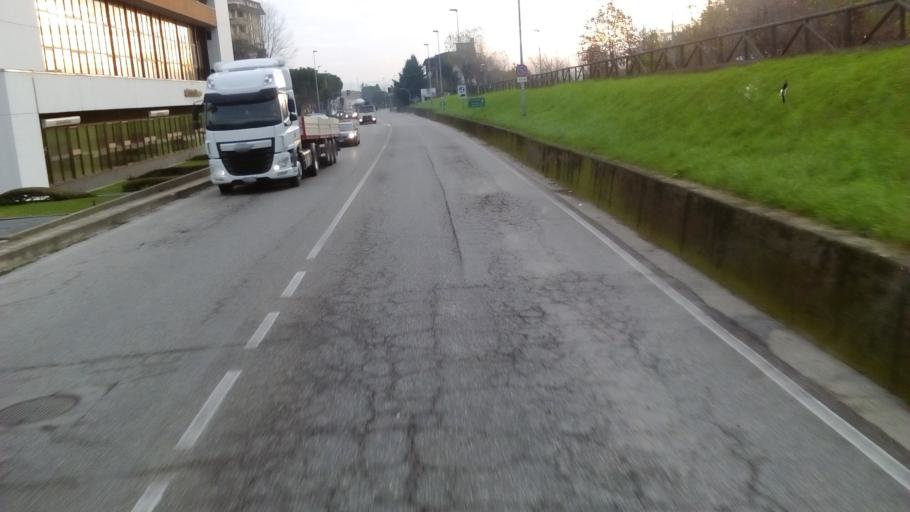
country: IT
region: Veneto
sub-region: Provincia di Vicenza
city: Arzignano
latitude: 45.5182
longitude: 11.3303
